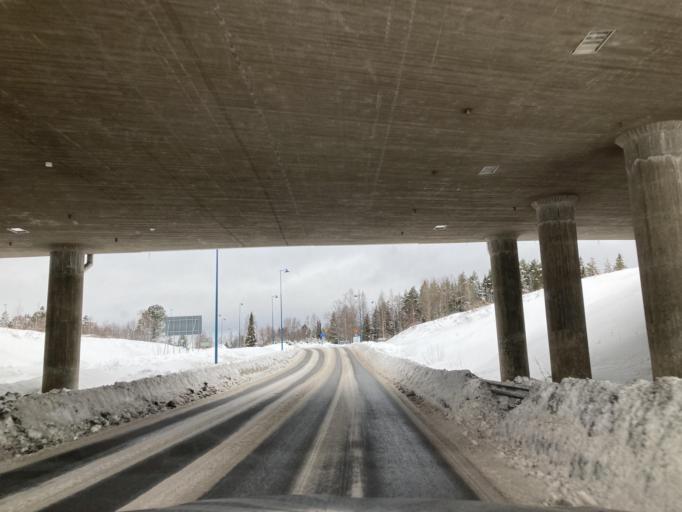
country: FI
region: Central Finland
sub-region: Jaemsae
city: Jaemsae
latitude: 61.8615
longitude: 25.2104
